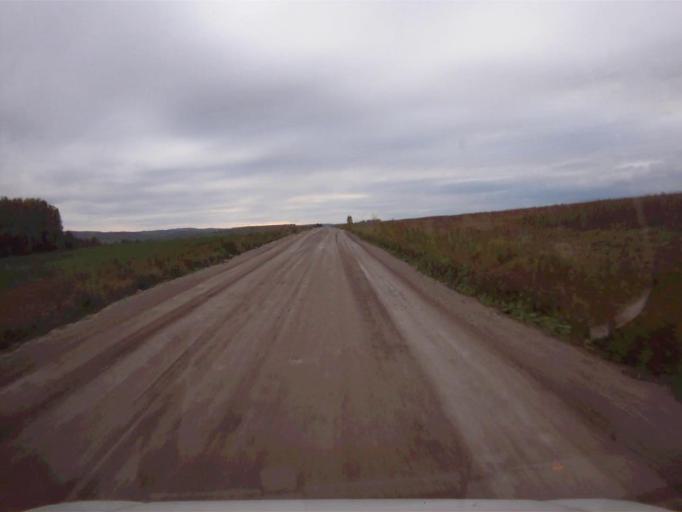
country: RU
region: Sverdlovsk
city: Mikhaylovsk
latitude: 56.1789
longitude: 59.2003
